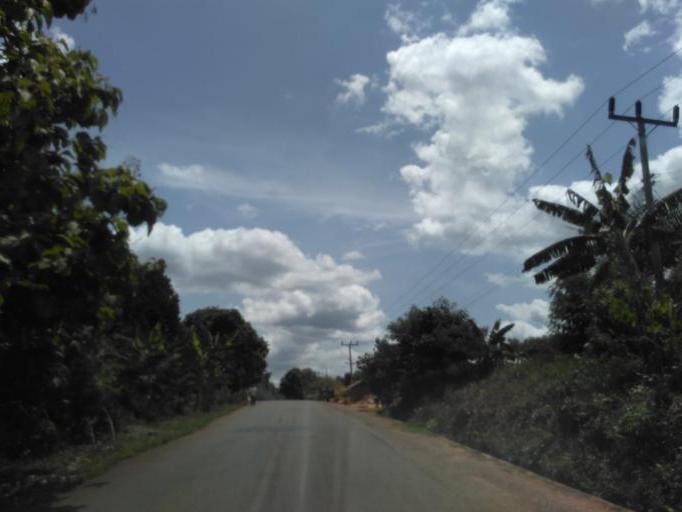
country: GH
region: Eastern
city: Koforidua
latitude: 6.1222
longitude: -0.1615
